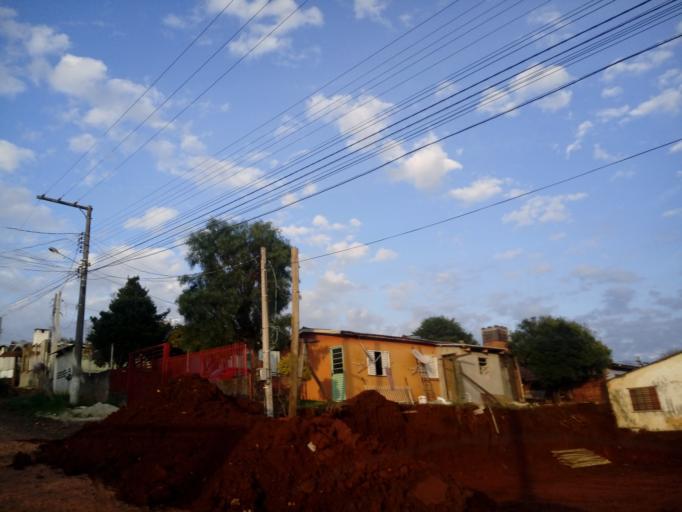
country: BR
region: Santa Catarina
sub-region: Chapeco
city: Chapeco
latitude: -27.1199
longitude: -52.6253
